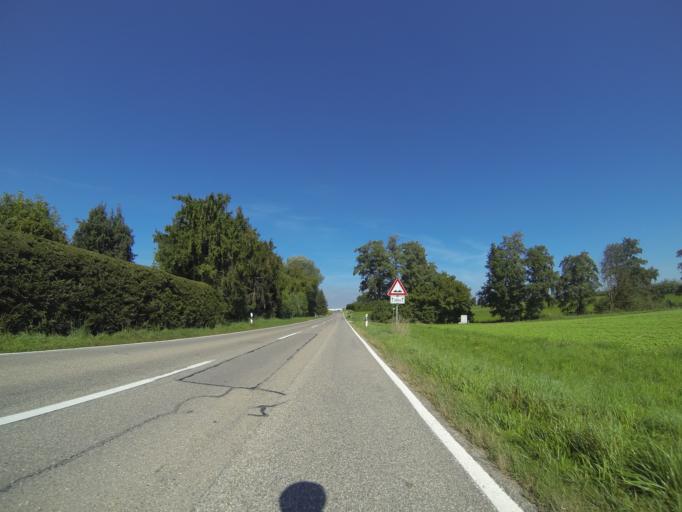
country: DE
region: Baden-Wuerttemberg
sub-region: Tuebingen Region
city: Erbach
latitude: 48.2968
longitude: 9.9073
